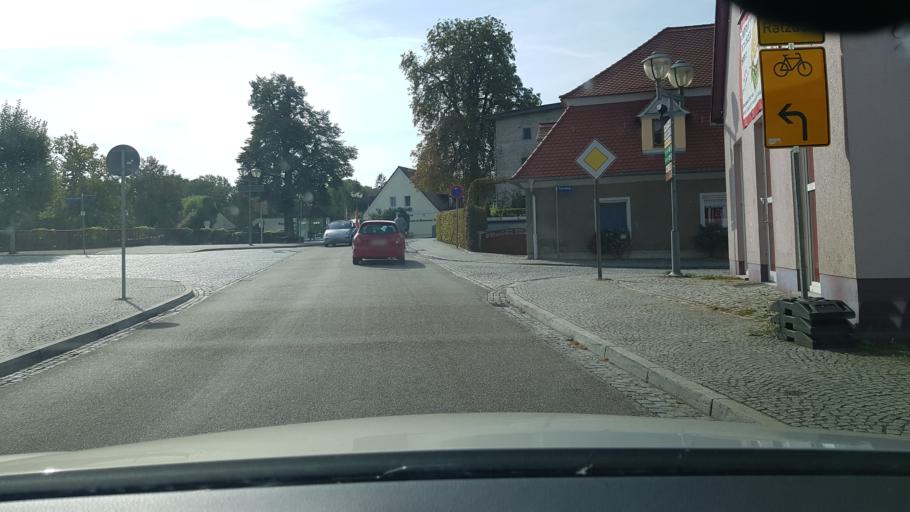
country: DE
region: Brandenburg
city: Neuzelle
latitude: 52.0912
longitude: 14.6491
